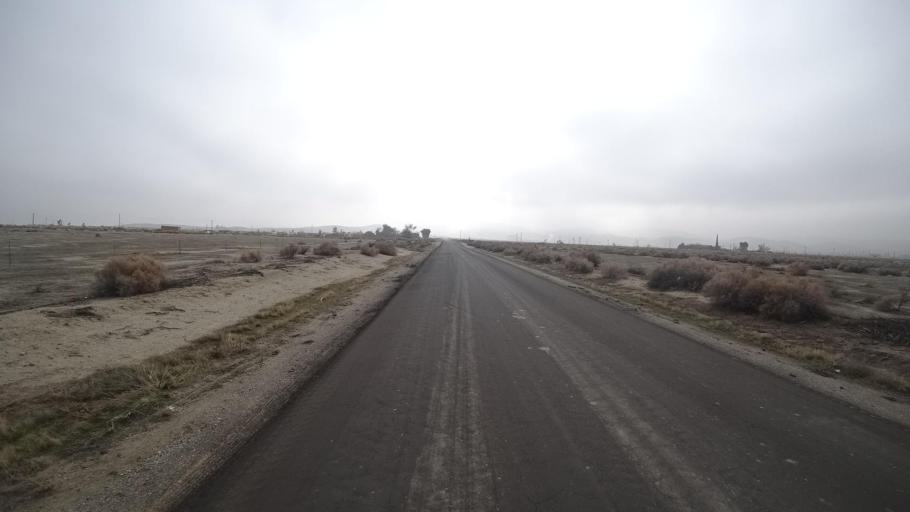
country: US
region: California
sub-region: Kern County
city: Maricopa
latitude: 35.0507
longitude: -119.3670
